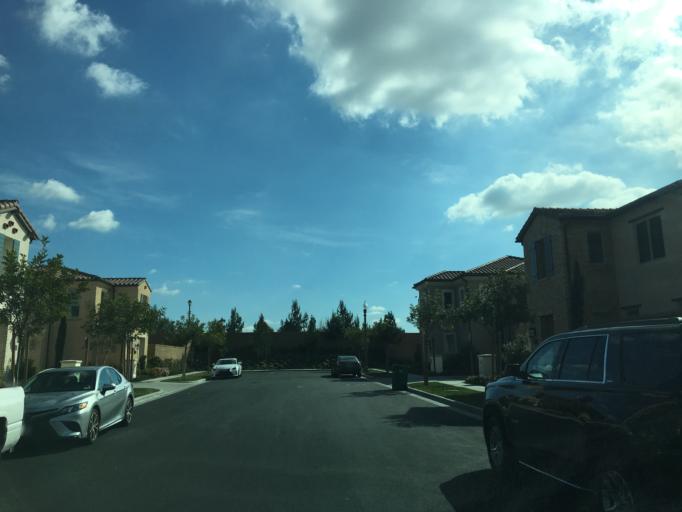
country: US
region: California
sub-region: Orange County
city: North Tustin
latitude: 33.7144
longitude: -117.7452
